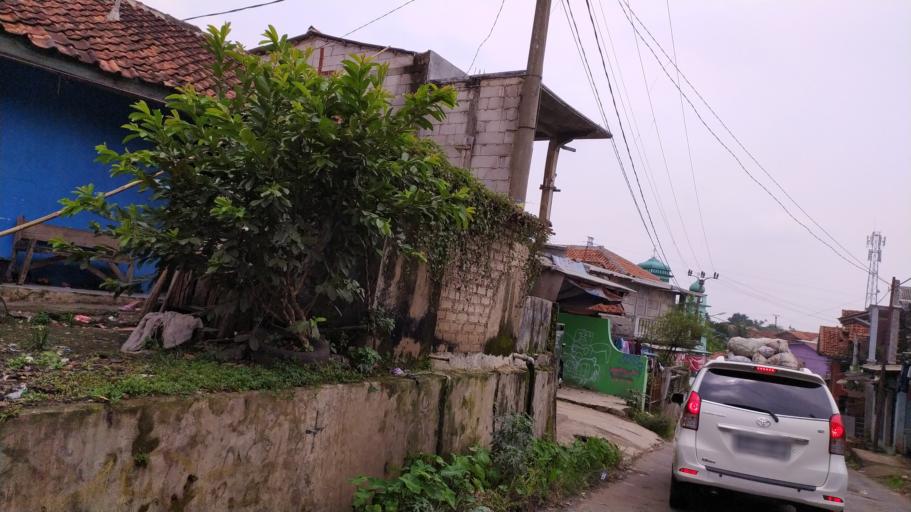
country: ID
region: West Java
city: Ciampea
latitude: -6.5920
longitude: 106.7043
